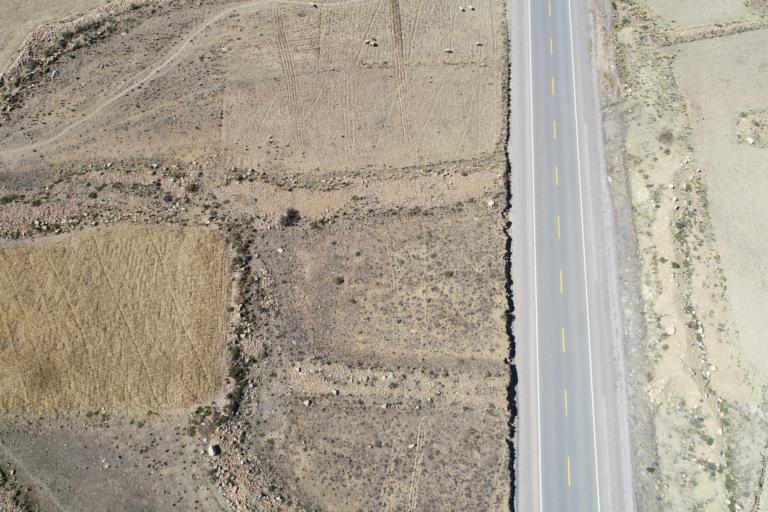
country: BO
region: La Paz
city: Achacachi
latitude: -15.8823
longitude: -68.8148
